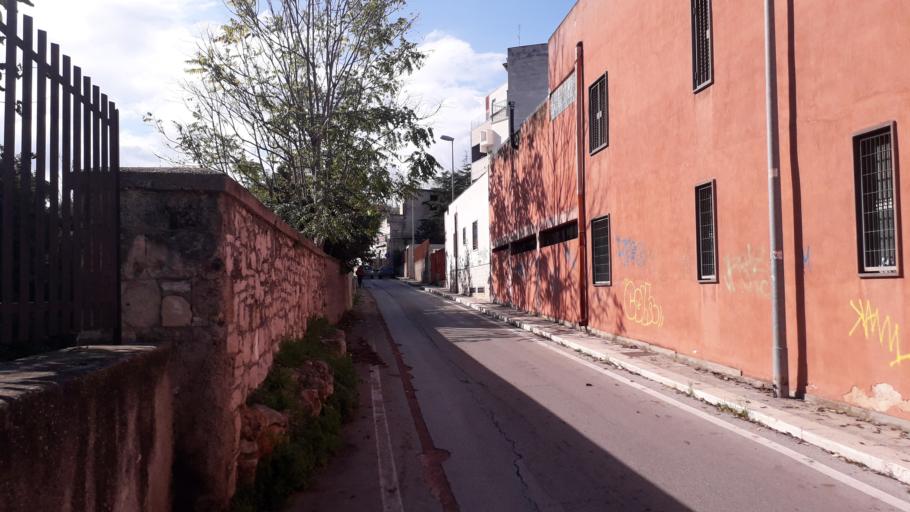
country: IT
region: Apulia
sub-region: Provincia di Bari
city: Bari
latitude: 41.1162
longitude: 16.8591
